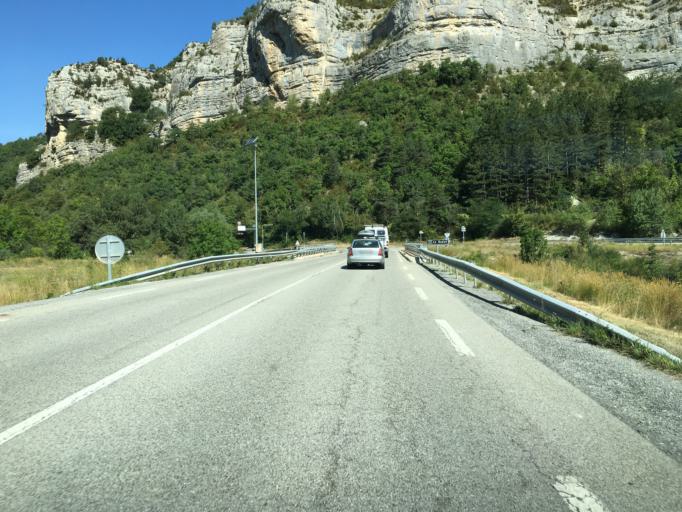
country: FR
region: Provence-Alpes-Cote d'Azur
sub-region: Departement des Hautes-Alpes
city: Veynes
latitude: 44.5508
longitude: 5.7762
